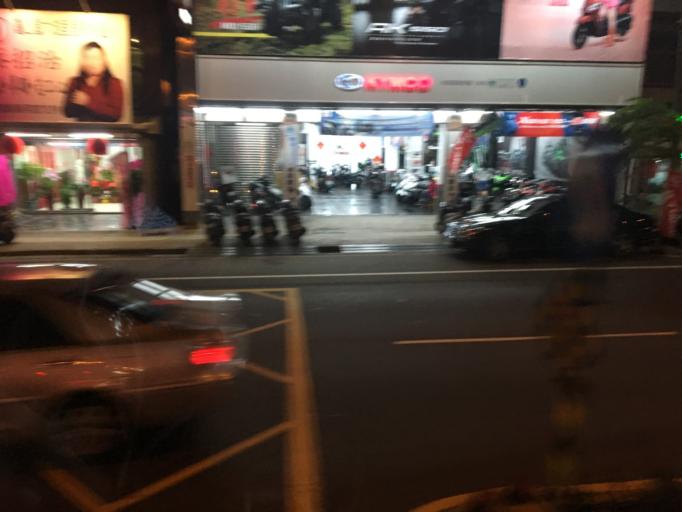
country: TW
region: Taiwan
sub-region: Taoyuan
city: Taoyuan
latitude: 25.0577
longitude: 121.3638
